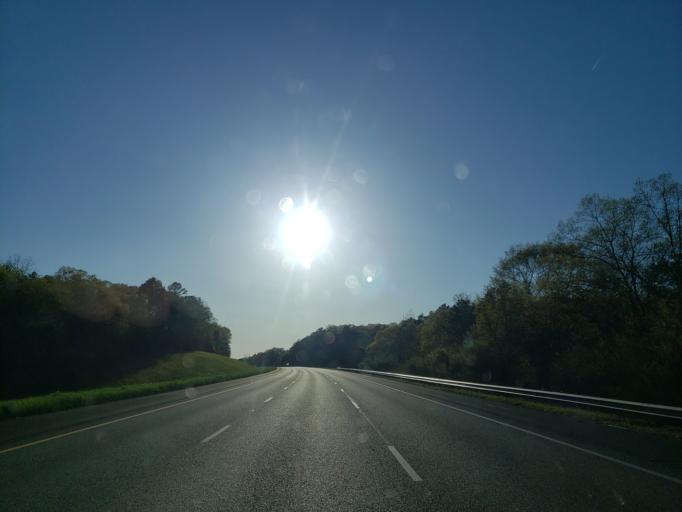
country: US
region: Alabama
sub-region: Calhoun County
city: Bynum
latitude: 33.5815
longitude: -85.9633
